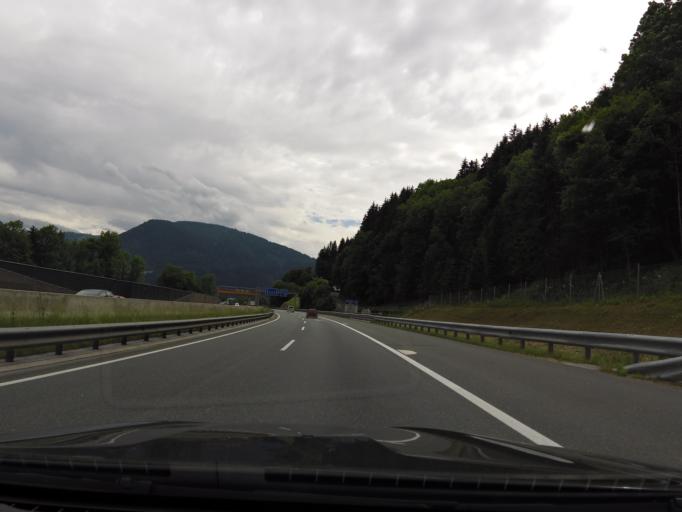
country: AT
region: Tyrol
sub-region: Politischer Bezirk Kufstein
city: Angath
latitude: 47.5030
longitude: 12.0579
